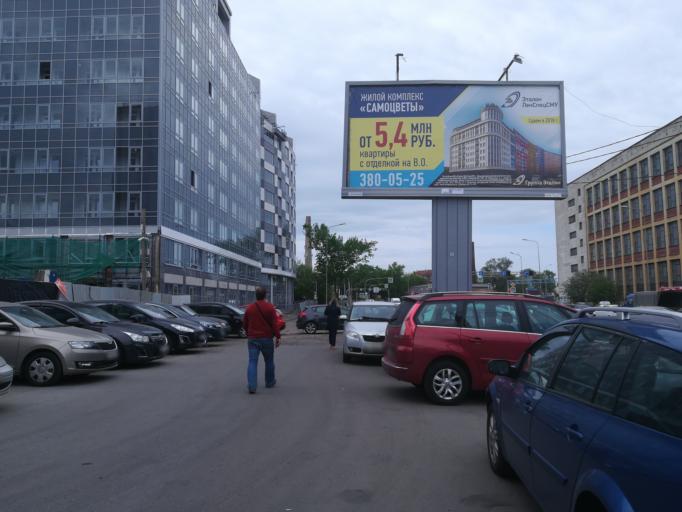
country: RU
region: St.-Petersburg
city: Vasyl'evsky Ostrov
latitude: 59.9508
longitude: 30.2663
